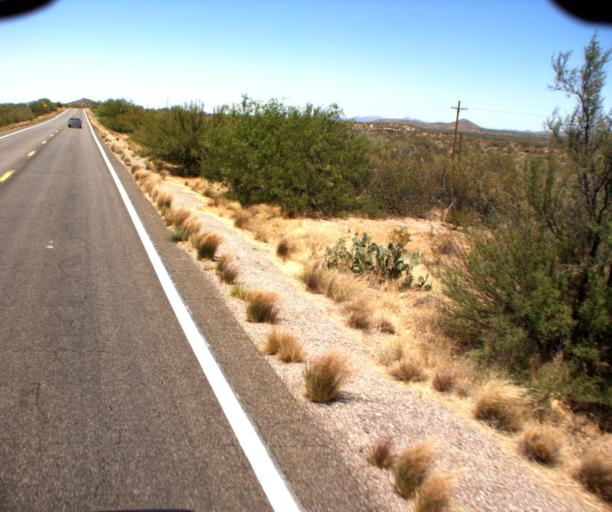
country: US
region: Arizona
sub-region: Pima County
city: Catalina
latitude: 32.6412
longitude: -111.0150
